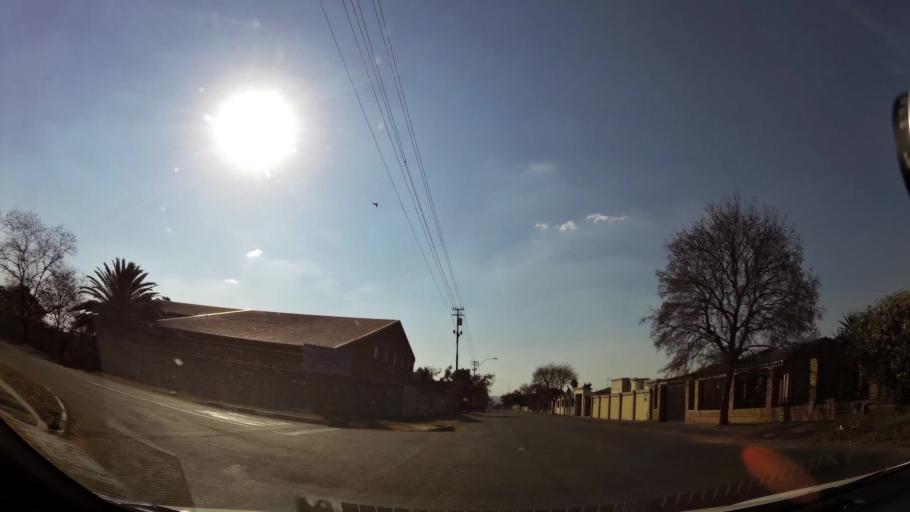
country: ZA
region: Gauteng
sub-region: City of Johannesburg Metropolitan Municipality
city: Johannesburg
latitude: -26.2544
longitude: 28.0064
